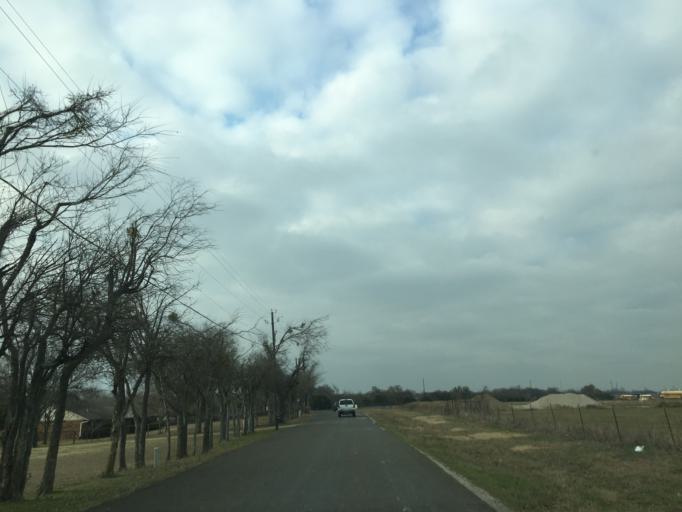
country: US
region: Texas
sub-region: Ellis County
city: Red Oak
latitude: 32.4928
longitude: -96.8025
